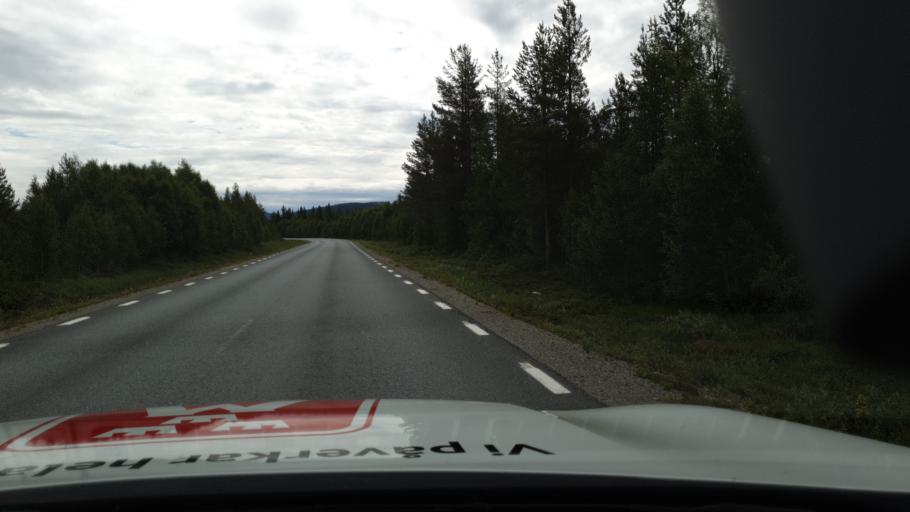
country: SE
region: Vaesterbotten
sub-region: Sorsele Kommun
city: Sorsele
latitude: 65.5222
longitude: 17.1702
